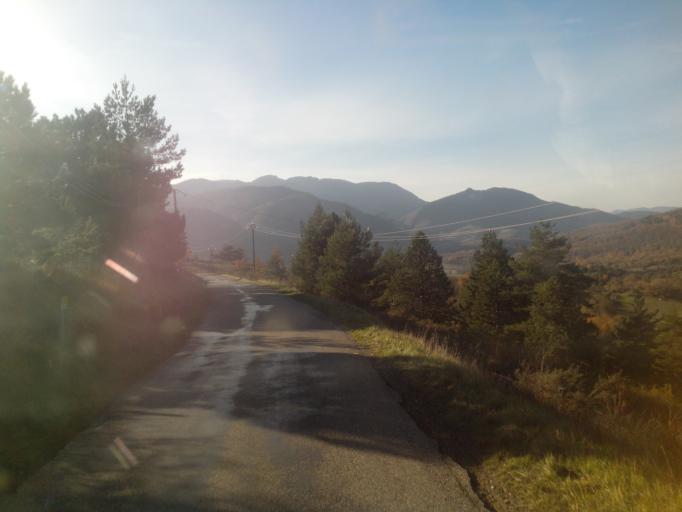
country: FR
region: Languedoc-Roussillon
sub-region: Departement de l'Aude
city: Couiza
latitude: 42.8779
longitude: 2.3668
